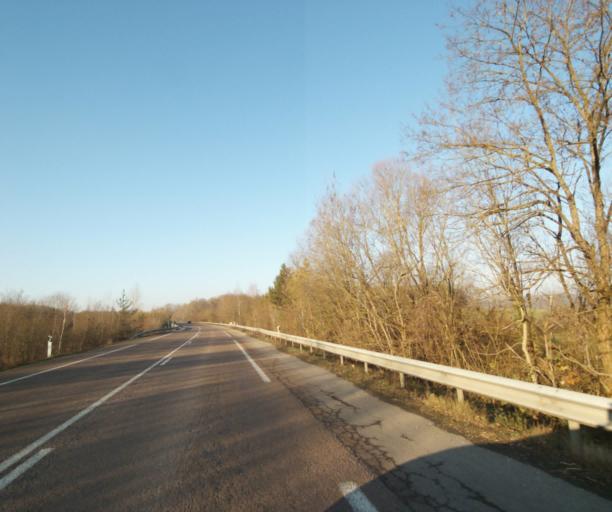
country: FR
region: Champagne-Ardenne
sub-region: Departement de la Haute-Marne
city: Chevillon
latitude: 48.4960
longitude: 5.1100
